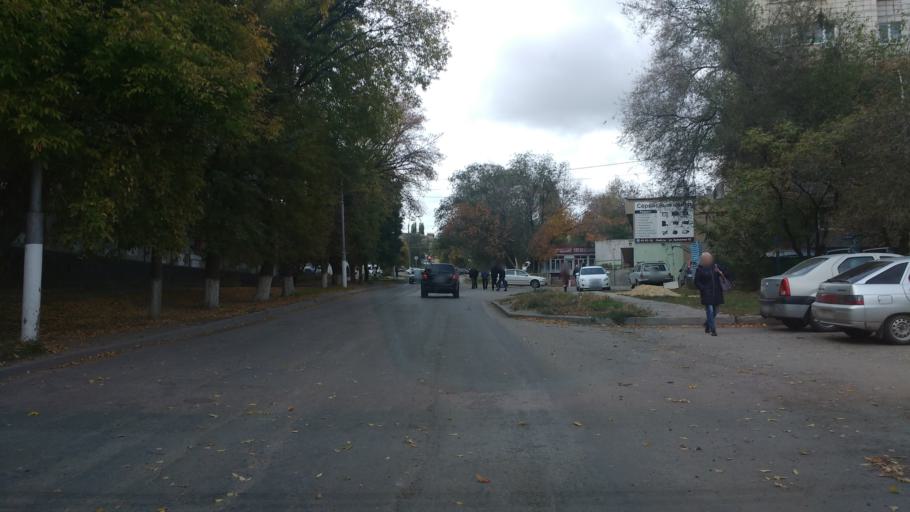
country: RU
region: Volgograd
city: Vodstroy
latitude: 48.7729
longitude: 44.5510
